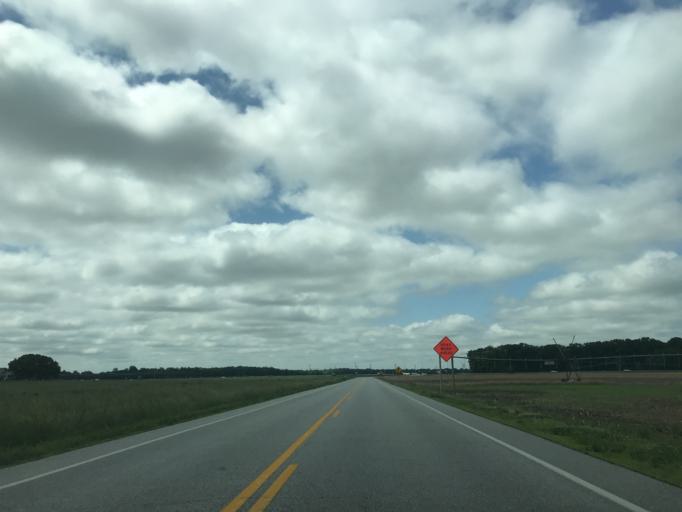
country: US
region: Maryland
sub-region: Caroline County
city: Ridgely
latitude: 38.9199
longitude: -75.8927
